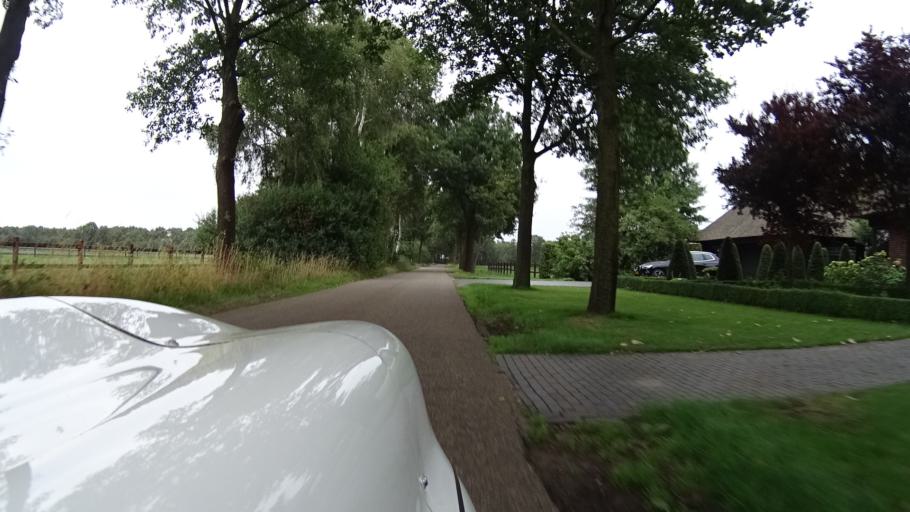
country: NL
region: North Brabant
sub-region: Gemeente Veghel
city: Erp
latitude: 51.6105
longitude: 5.6258
